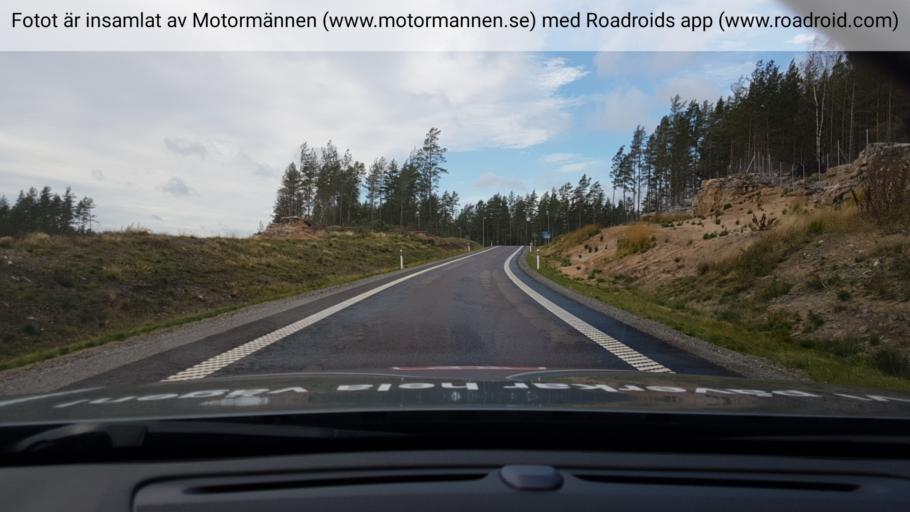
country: SE
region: Vaermland
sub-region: Kils Kommun
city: Kil
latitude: 59.3850
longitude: 13.3395
